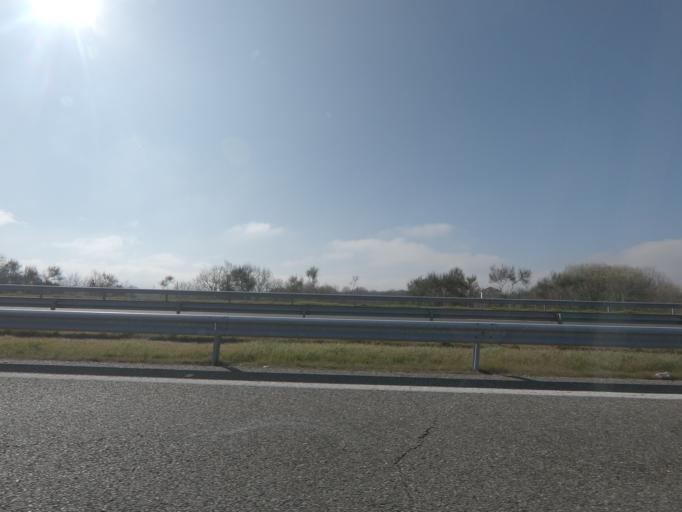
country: ES
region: Galicia
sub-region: Provincia de Ourense
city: Taboadela
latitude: 42.2115
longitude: -7.8347
